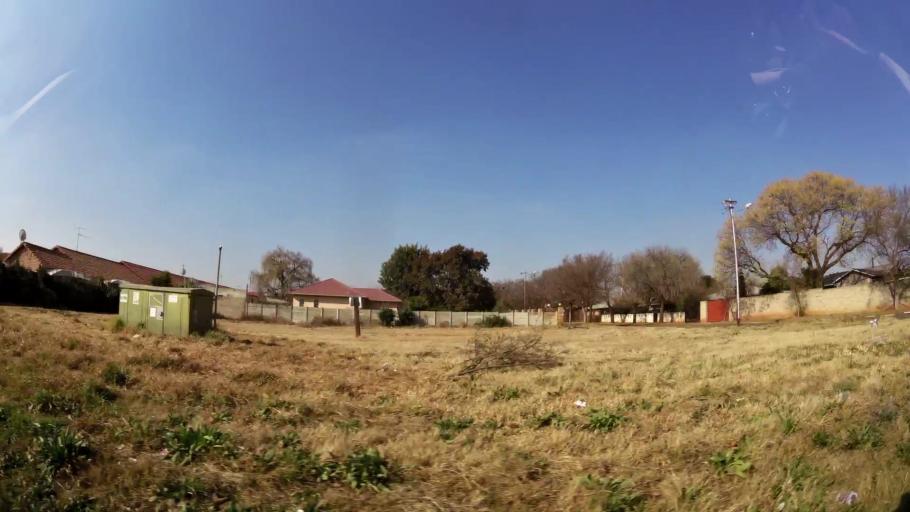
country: ZA
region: Gauteng
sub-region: West Rand District Municipality
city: Randfontein
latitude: -26.1811
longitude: 27.6925
